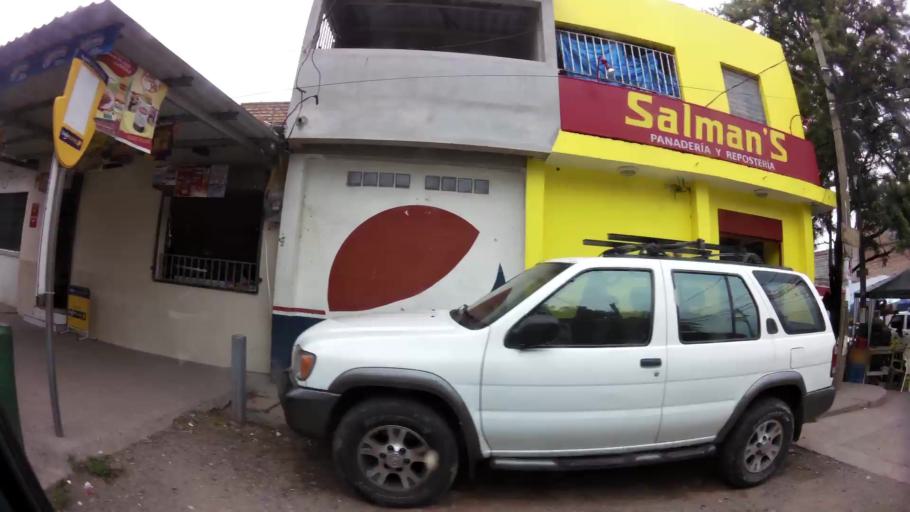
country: HN
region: Francisco Morazan
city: Tegucigalpa
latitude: 14.0742
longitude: -87.1683
